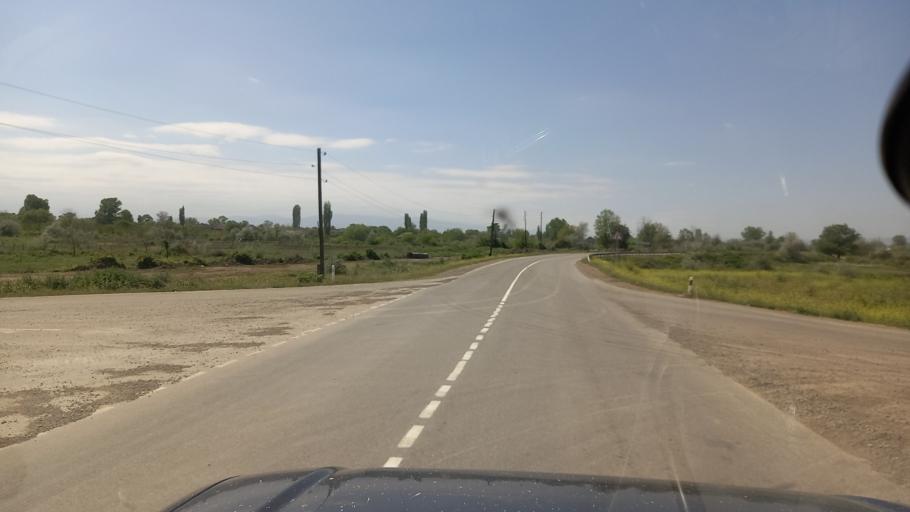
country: RU
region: Dagestan
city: Novaya Maka
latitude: 41.8099
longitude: 48.4076
